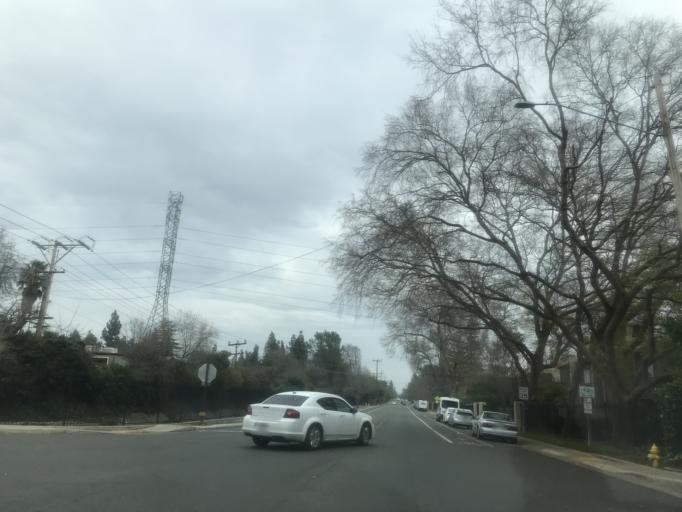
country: US
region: California
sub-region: Sacramento County
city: Arden-Arcade
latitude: 38.5816
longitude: -121.4110
